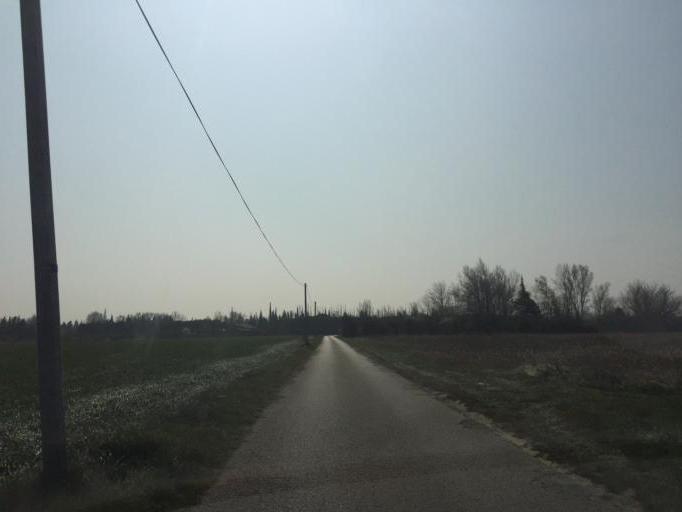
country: FR
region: Provence-Alpes-Cote d'Azur
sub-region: Departement du Vaucluse
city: Jonquieres
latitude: 44.1018
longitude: 4.8999
